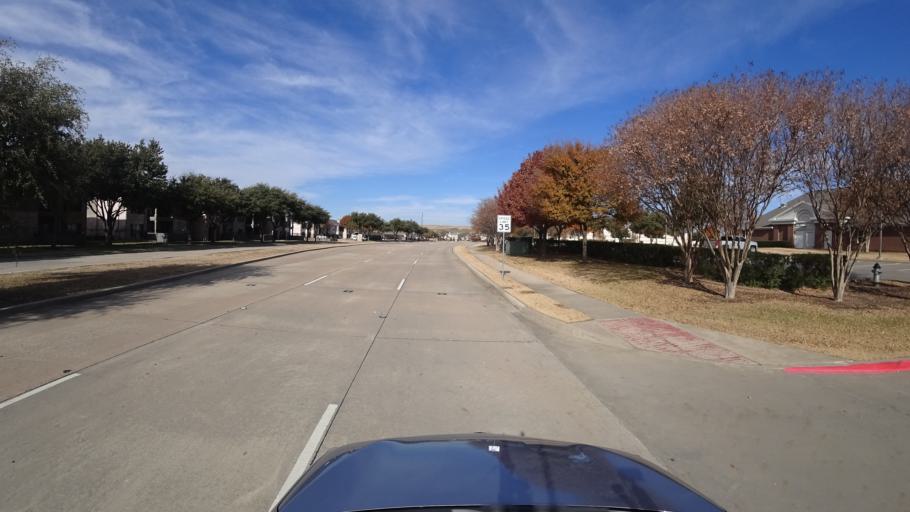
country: US
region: Texas
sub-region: Denton County
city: Lewisville
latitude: 33.0129
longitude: -96.9441
